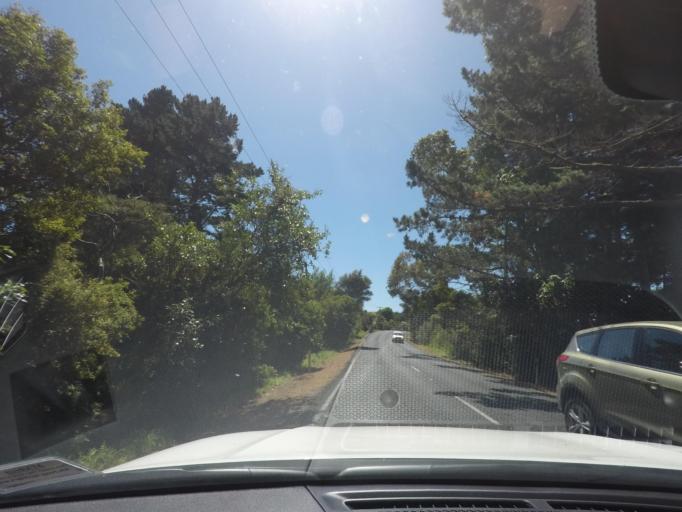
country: NZ
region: Auckland
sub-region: Auckland
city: Parakai
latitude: -36.6097
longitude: 174.3359
